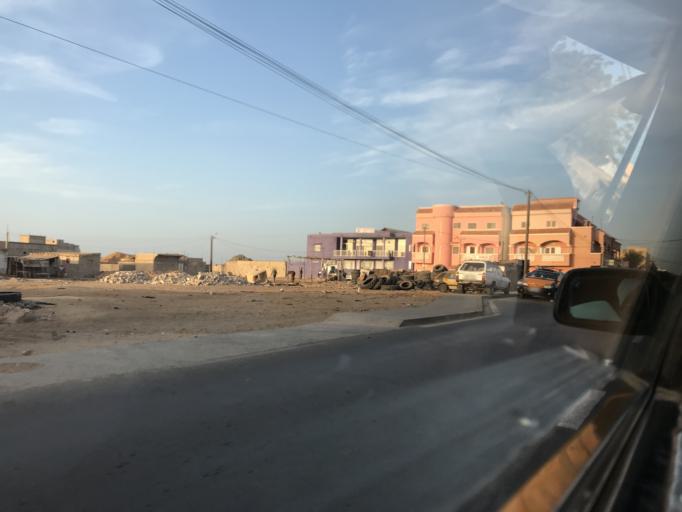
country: SN
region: Saint-Louis
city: Saint-Louis
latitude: 16.0263
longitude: -16.4813
